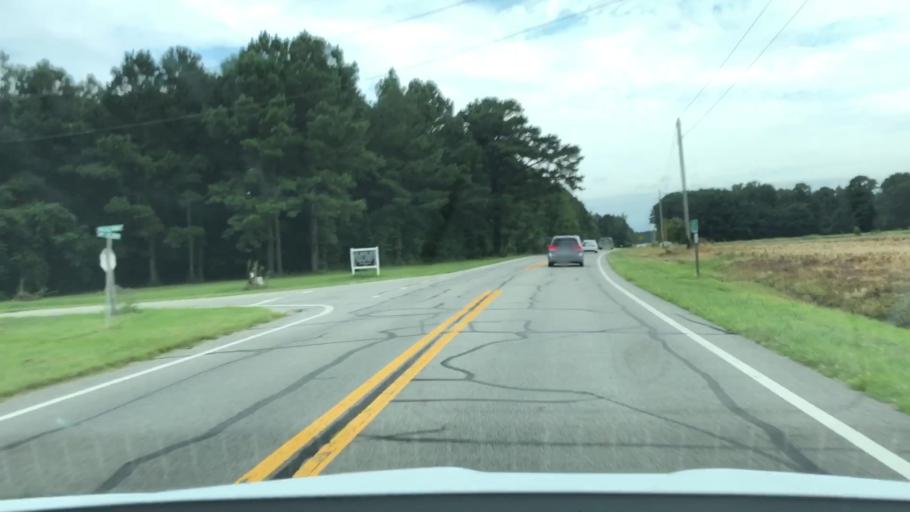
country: US
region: North Carolina
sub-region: Lenoir County
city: Kinston
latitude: 35.1623
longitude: -77.5560
